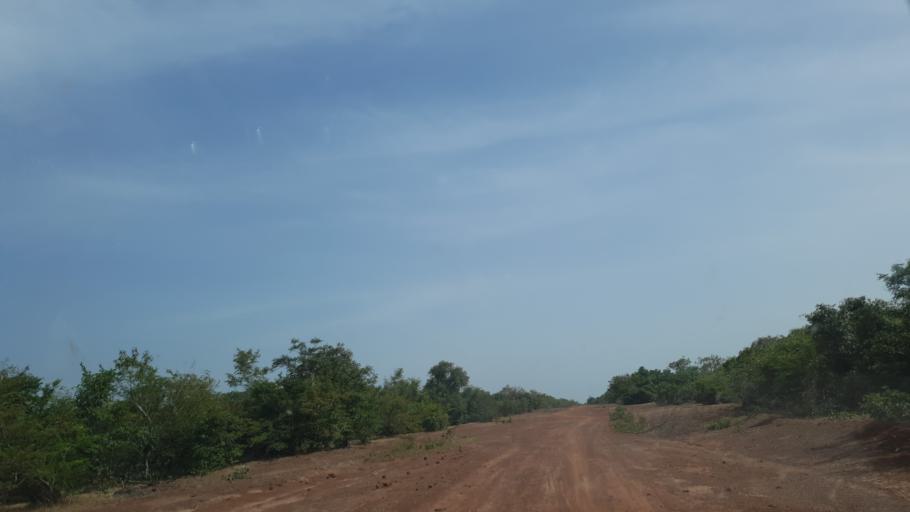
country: ML
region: Koulikoro
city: Dioila
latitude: 12.4367
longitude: -6.2117
